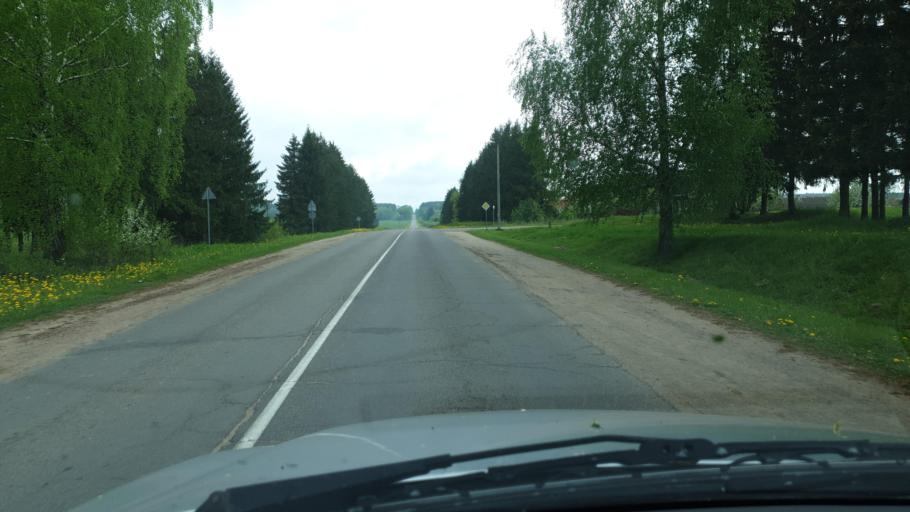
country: BY
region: Vitebsk
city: Lyepyel'
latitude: 54.8887
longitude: 28.6207
